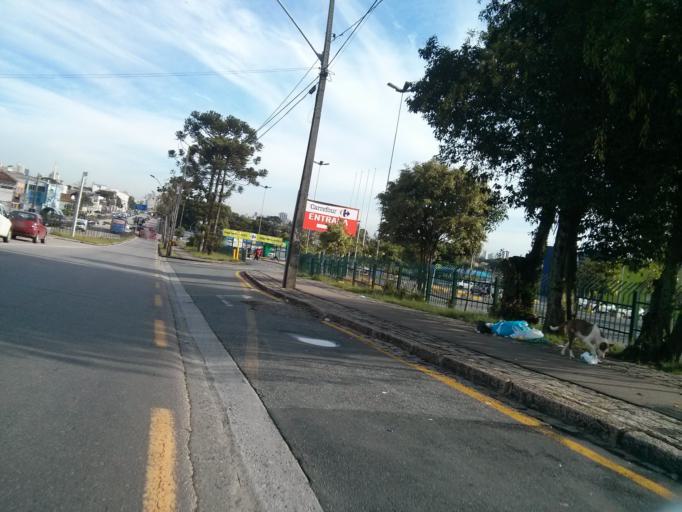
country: BR
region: Parana
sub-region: Curitiba
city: Curitiba
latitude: -25.4563
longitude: -49.2594
